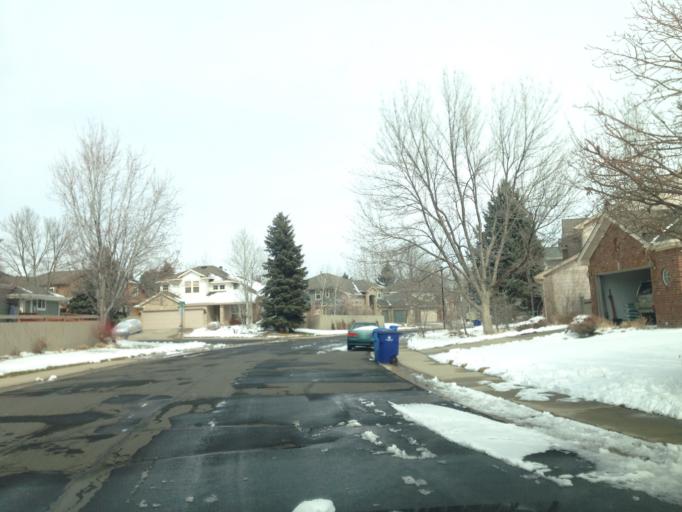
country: US
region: Colorado
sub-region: Boulder County
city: Lafayette
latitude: 39.9710
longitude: -105.0993
